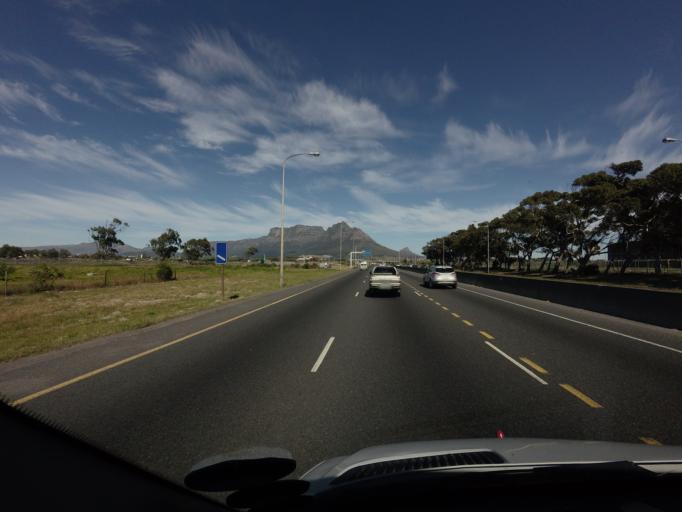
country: ZA
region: Western Cape
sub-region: City of Cape Town
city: Lansdowne
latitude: -33.9502
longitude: 18.5168
